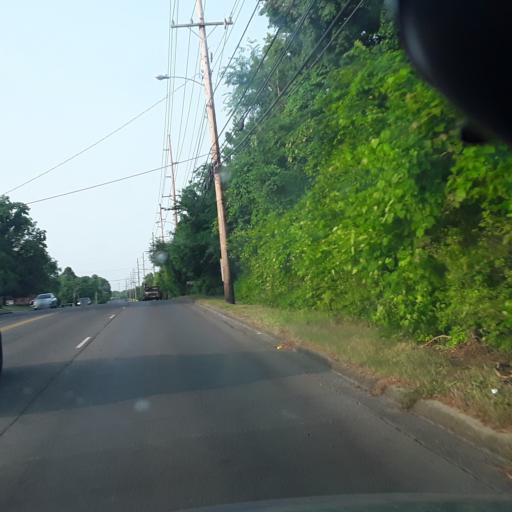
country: US
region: Tennessee
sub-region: Williamson County
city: Brentwood
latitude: 36.0506
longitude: -86.7434
